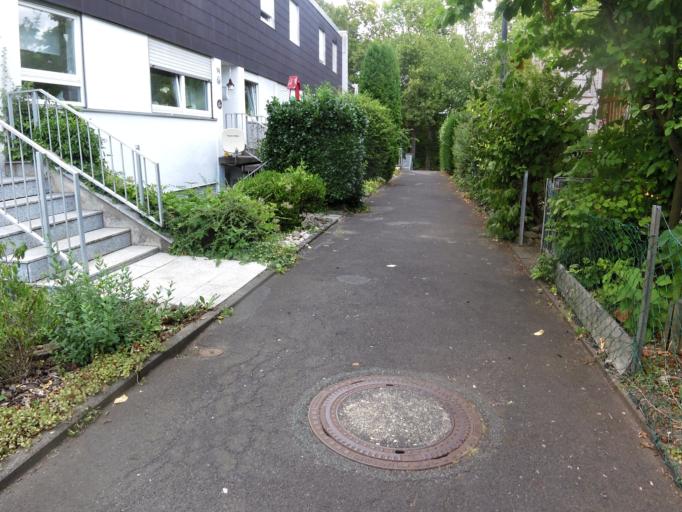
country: DE
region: Bavaria
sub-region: Regierungsbezirk Unterfranken
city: Hochberg
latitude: 49.7908
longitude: 9.8881
